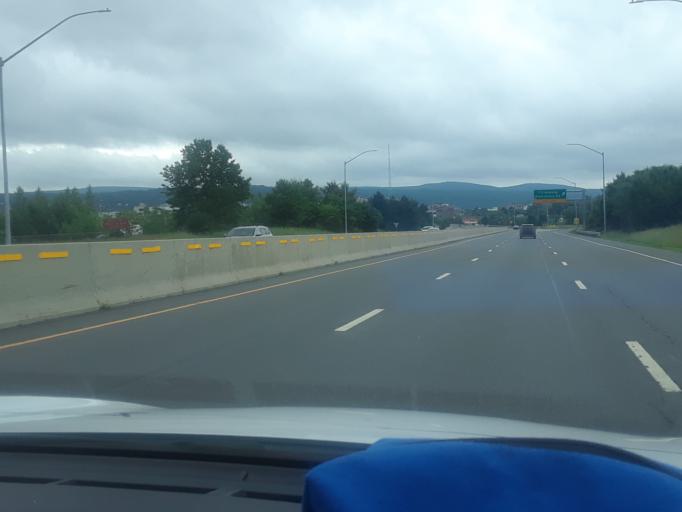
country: US
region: Pennsylvania
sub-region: Lackawanna County
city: Scranton
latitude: 41.4204
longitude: -75.6709
